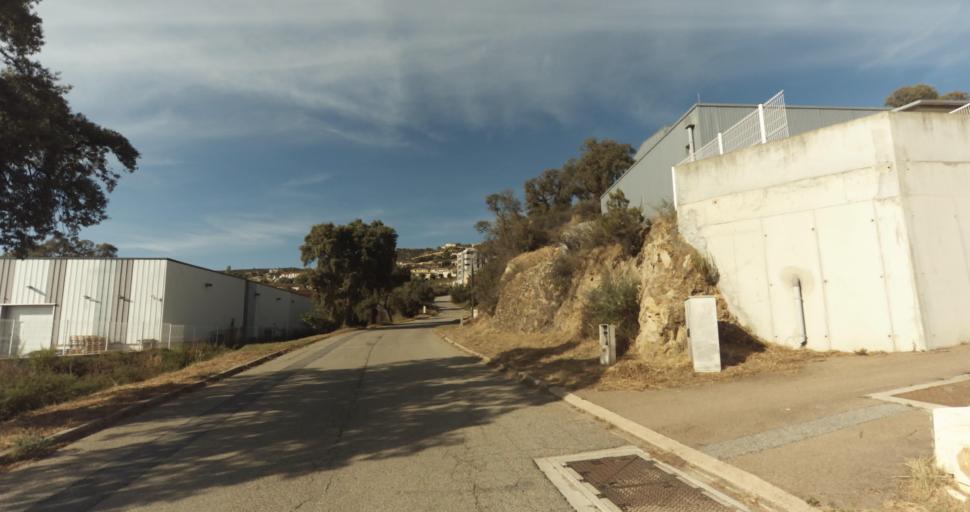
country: FR
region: Corsica
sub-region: Departement de la Corse-du-Sud
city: Afa
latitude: 41.9321
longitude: 8.7909
